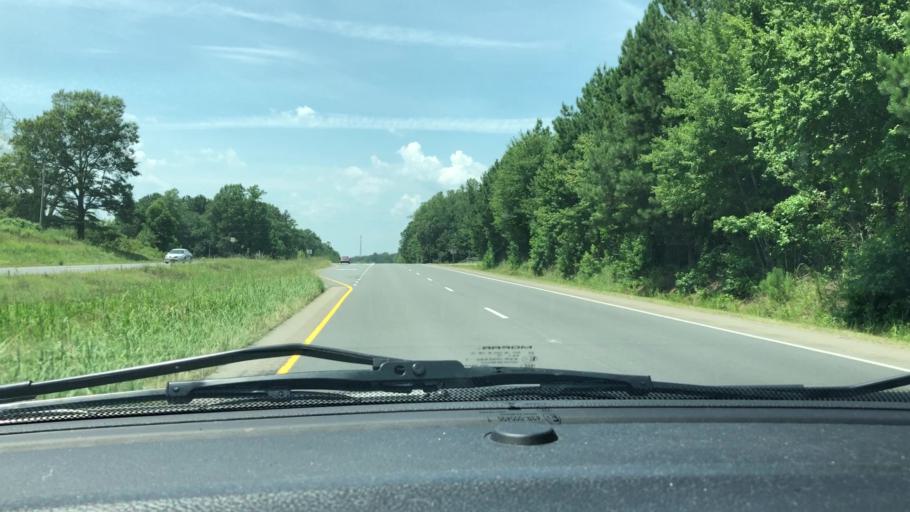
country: US
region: North Carolina
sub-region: Chatham County
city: Siler City
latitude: 35.6361
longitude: -79.3732
